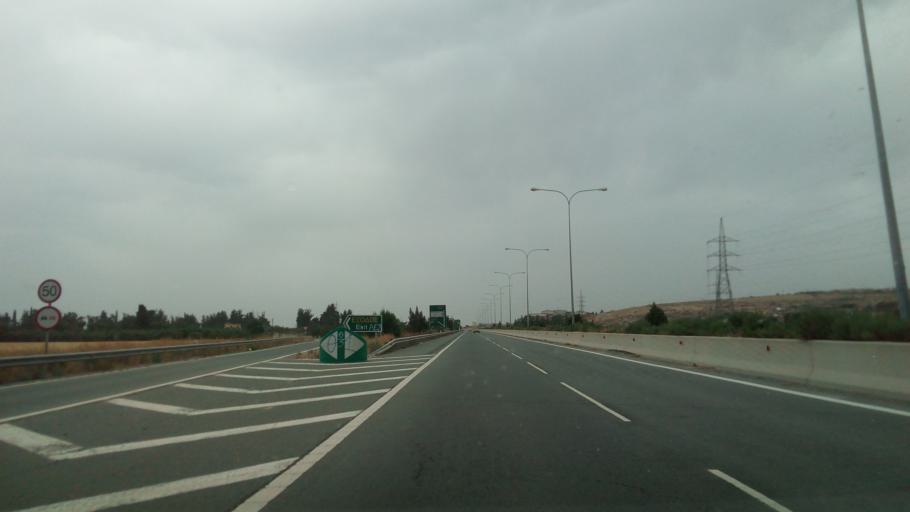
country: CY
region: Pafos
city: Mesogi
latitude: 34.7454
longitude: 32.5072
